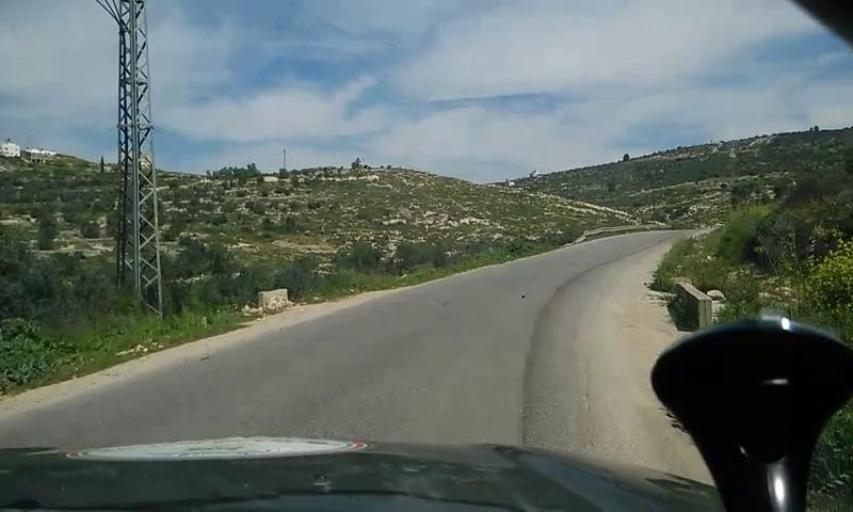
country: PS
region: West Bank
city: Bayt `Ur at Tahta
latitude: 31.8888
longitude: 35.0842
